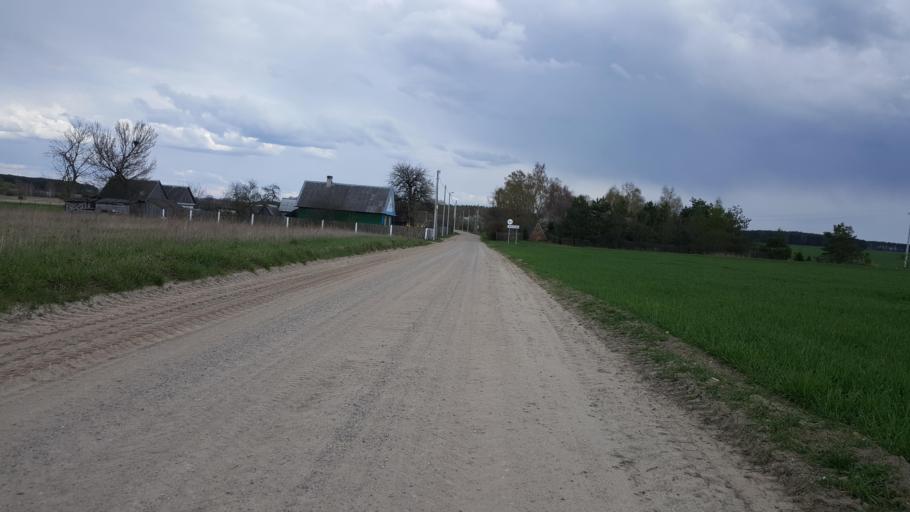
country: BY
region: Brest
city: Kamyanyets
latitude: 52.4024
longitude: 23.7259
